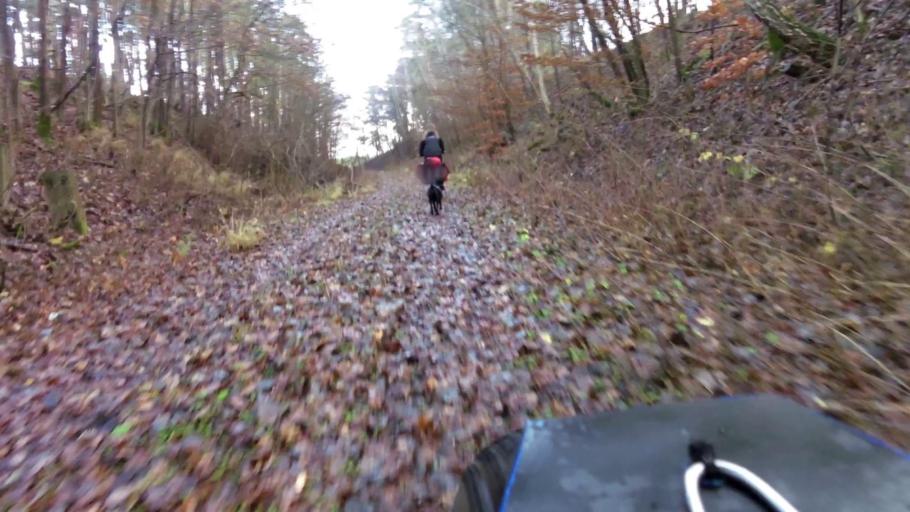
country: PL
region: Lubusz
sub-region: Powiat gorzowski
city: Jenin
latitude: 52.7254
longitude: 15.1356
